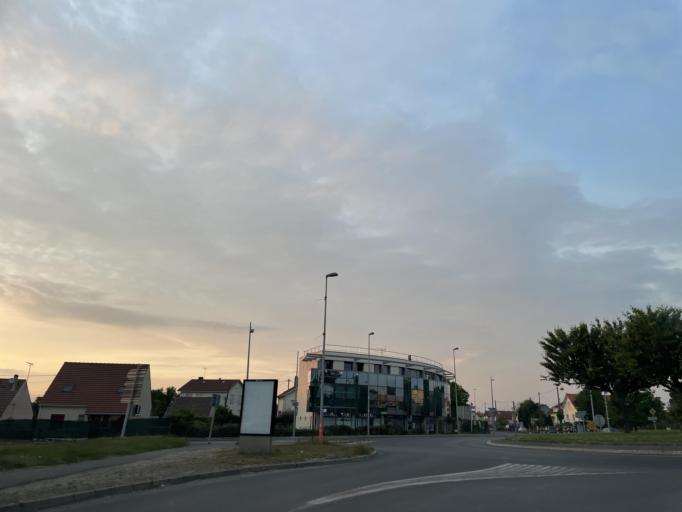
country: FR
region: Ile-de-France
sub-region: Departement de Seine-et-Marne
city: Meaux
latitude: 48.9419
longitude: 2.8792
